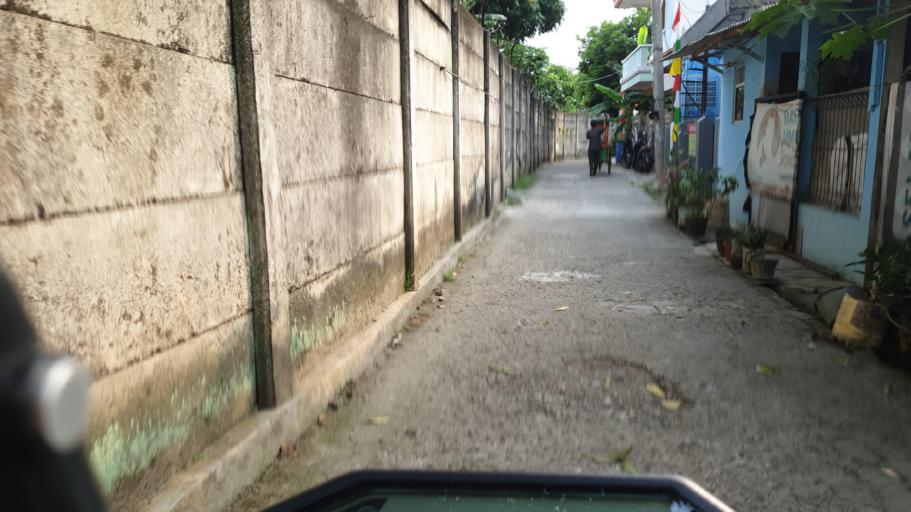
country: ID
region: West Java
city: Depok
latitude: -6.3406
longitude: 106.8298
